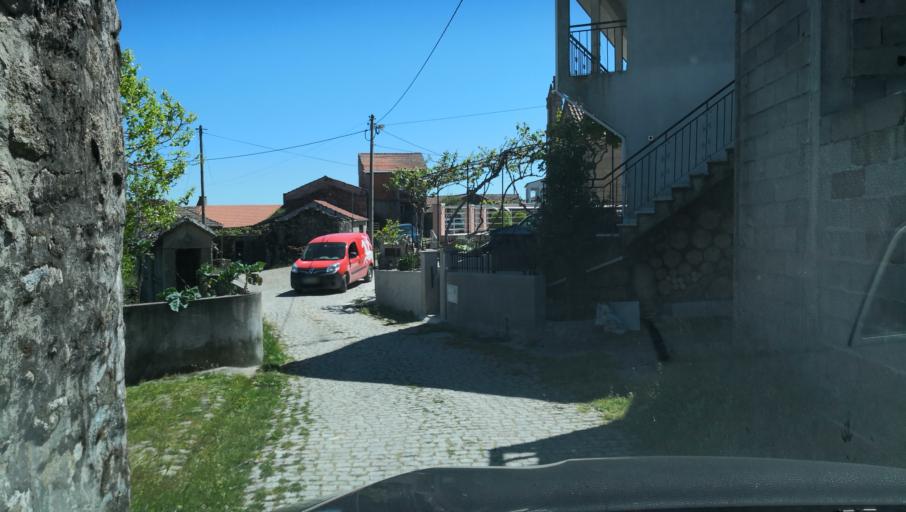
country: PT
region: Vila Real
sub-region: Sabrosa
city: Sabrosa
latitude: 41.3163
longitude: -7.6425
